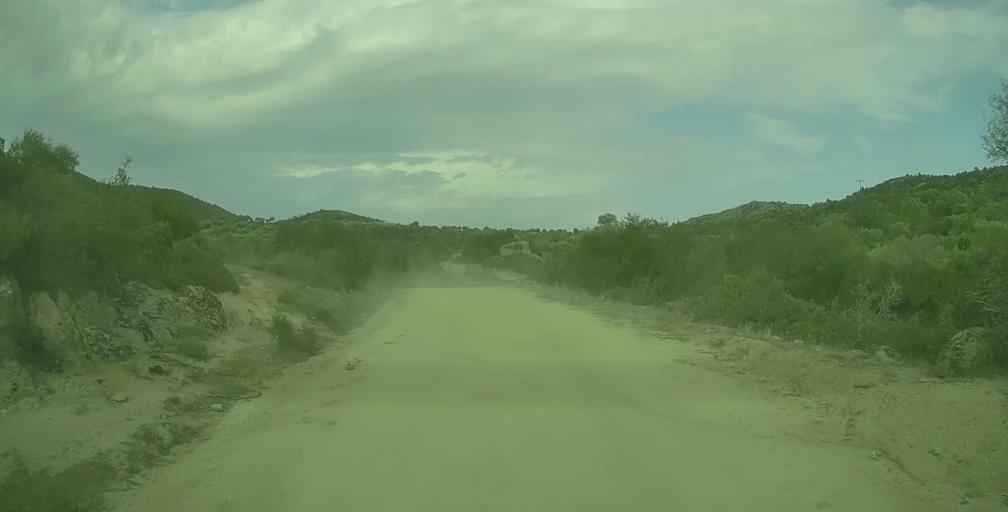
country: GR
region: Central Macedonia
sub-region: Nomos Chalkidikis
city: Sykia
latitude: 40.0114
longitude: 23.9288
